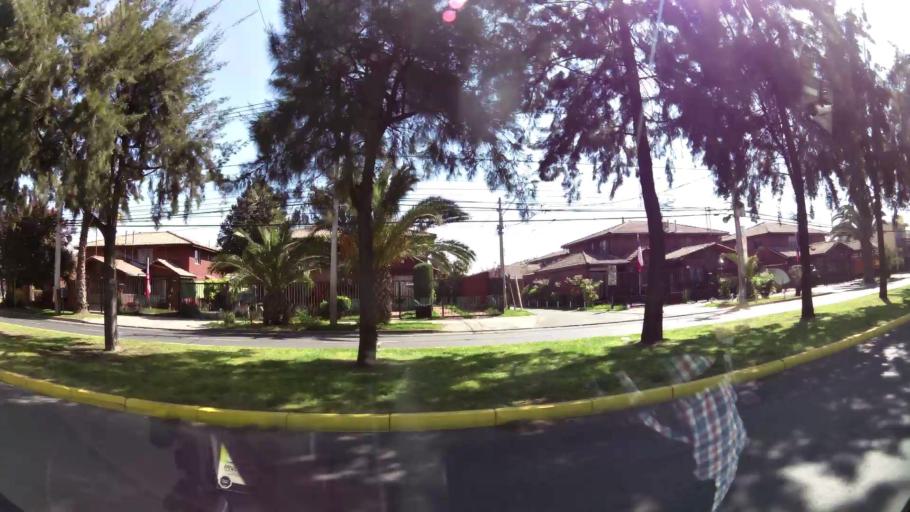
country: CL
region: Santiago Metropolitan
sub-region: Provincia de Santiago
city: Lo Prado
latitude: -33.3523
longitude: -70.7289
